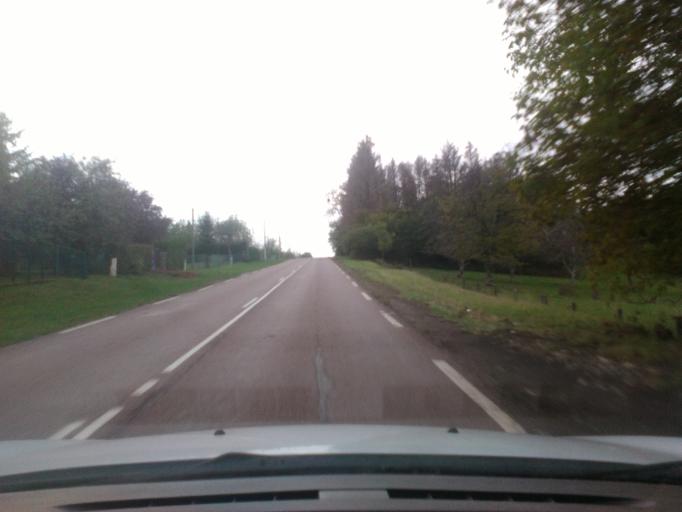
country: FR
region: Lorraine
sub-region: Departement des Vosges
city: Chatel-sur-Moselle
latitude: 48.3489
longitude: 6.4126
